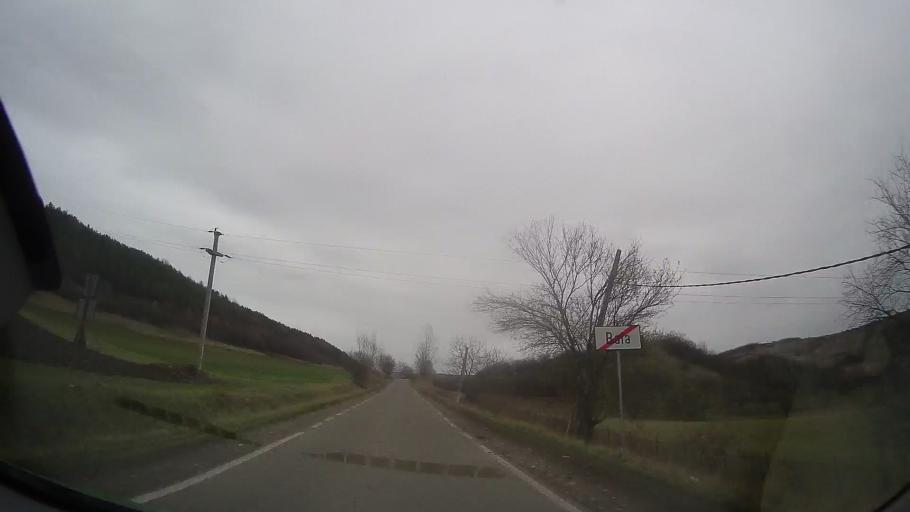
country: RO
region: Mures
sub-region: Comuna Bala
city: Bala
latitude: 46.7143
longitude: 24.5067
